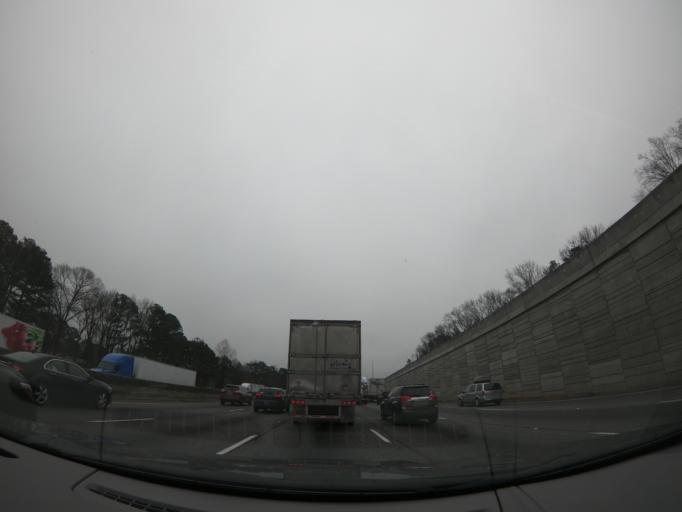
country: US
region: Georgia
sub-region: Cobb County
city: Smyrna
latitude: 33.9336
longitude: -84.4933
